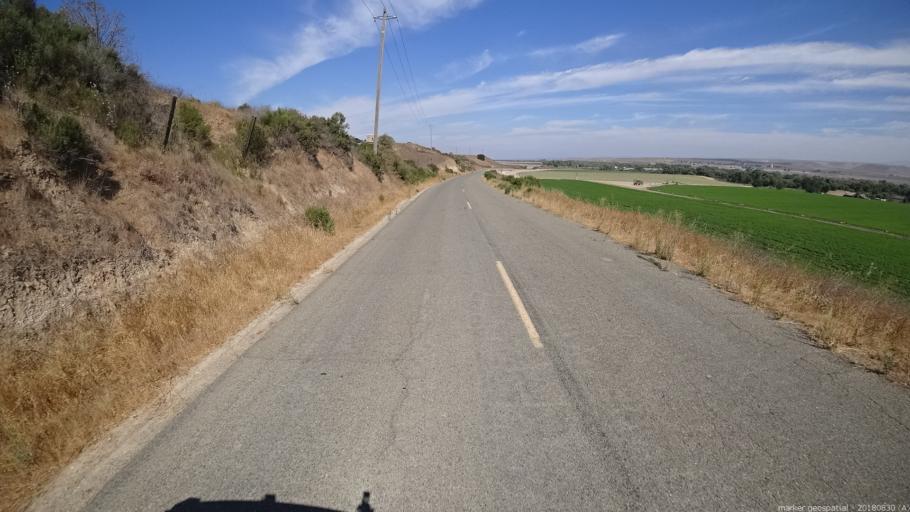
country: US
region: California
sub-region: Monterey County
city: King City
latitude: 36.0984
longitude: -121.0214
